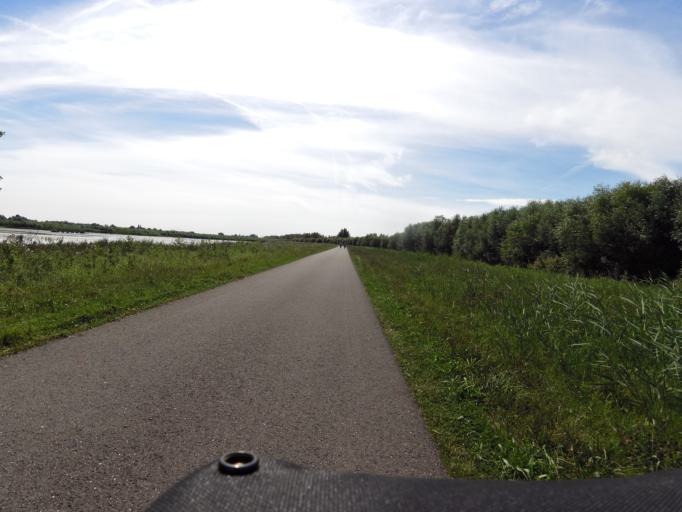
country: NL
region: South Holland
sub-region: Gemeente Sliedrecht
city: Sliedrecht
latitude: 51.7749
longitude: 4.7584
